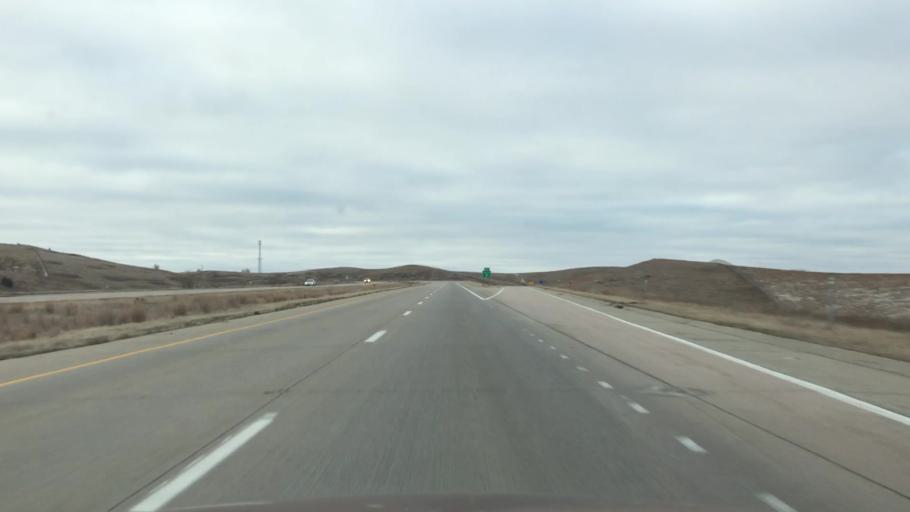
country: US
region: Iowa
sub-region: Woodbury County
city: Sioux City
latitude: 42.5243
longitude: -96.3394
